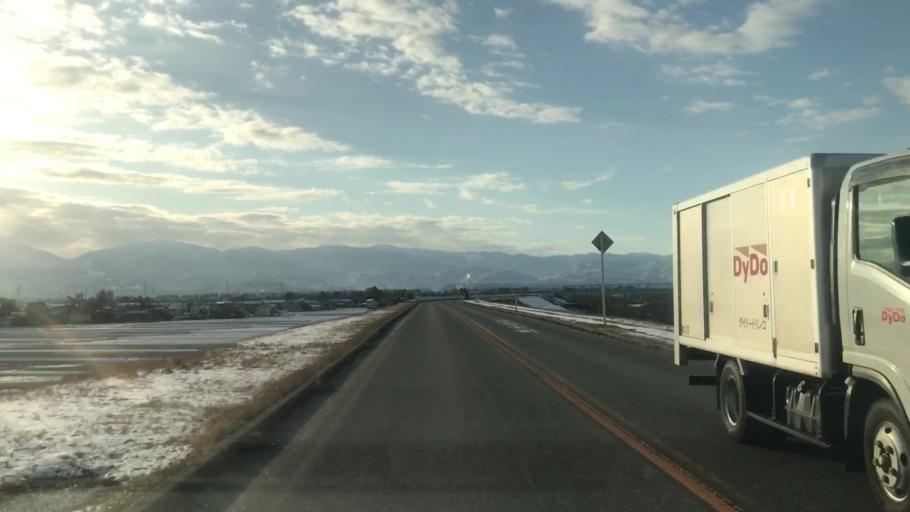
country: JP
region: Toyama
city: Toyama-shi
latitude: 36.6790
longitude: 137.2846
